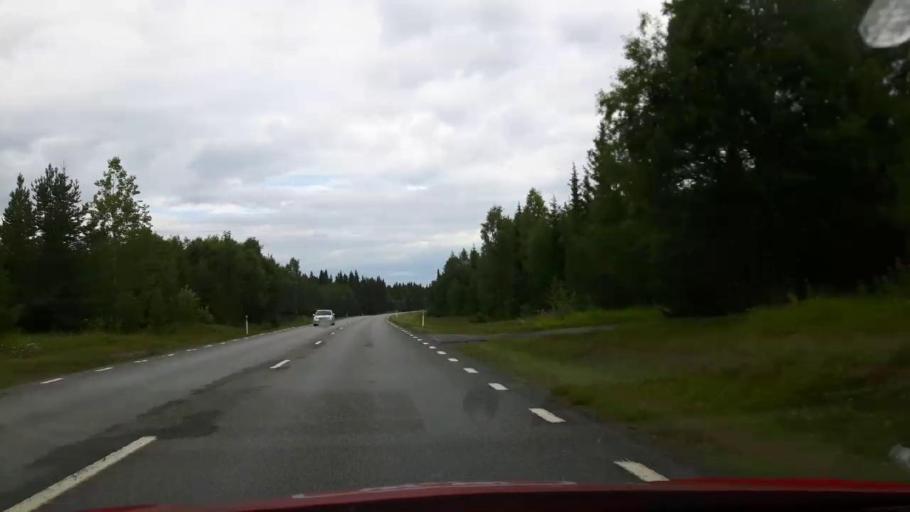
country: SE
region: Jaemtland
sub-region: Stroemsunds Kommun
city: Stroemsund
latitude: 63.6141
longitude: 15.3571
